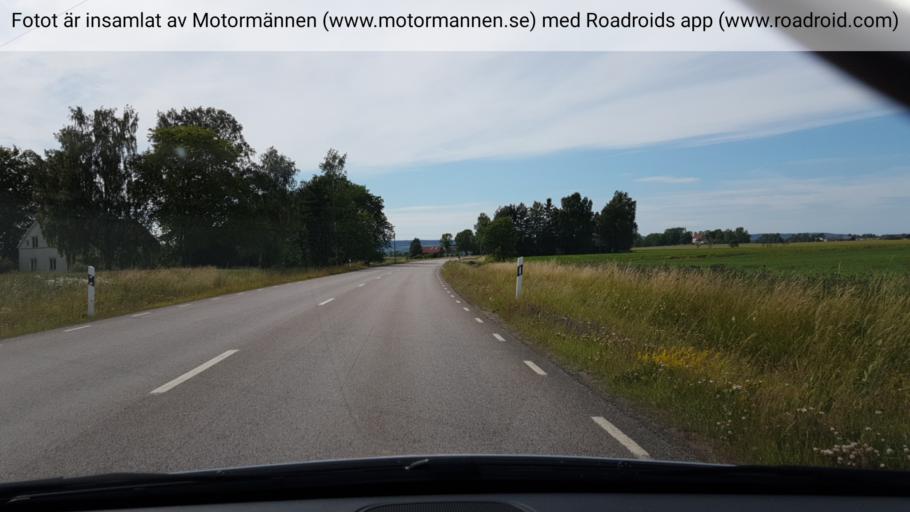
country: SE
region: Vaestra Goetaland
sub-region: Skovde Kommun
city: Skoevde
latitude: 58.3831
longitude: 13.9498
